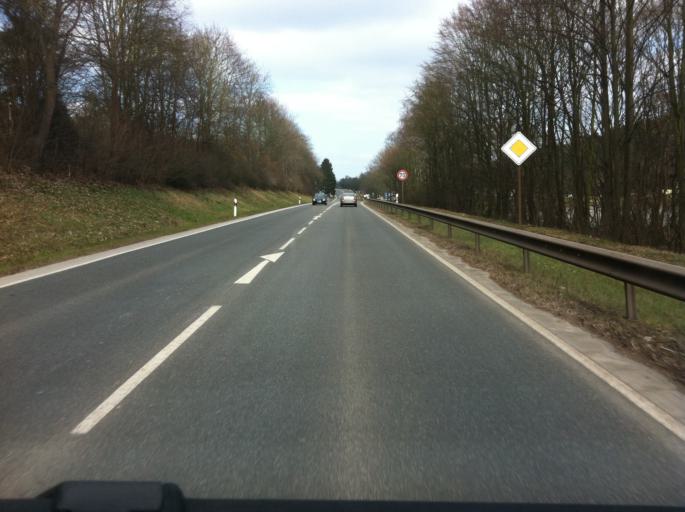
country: DE
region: North Rhine-Westphalia
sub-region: Regierungsbezirk Koln
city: Mechernich
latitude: 50.6038
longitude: 6.6350
